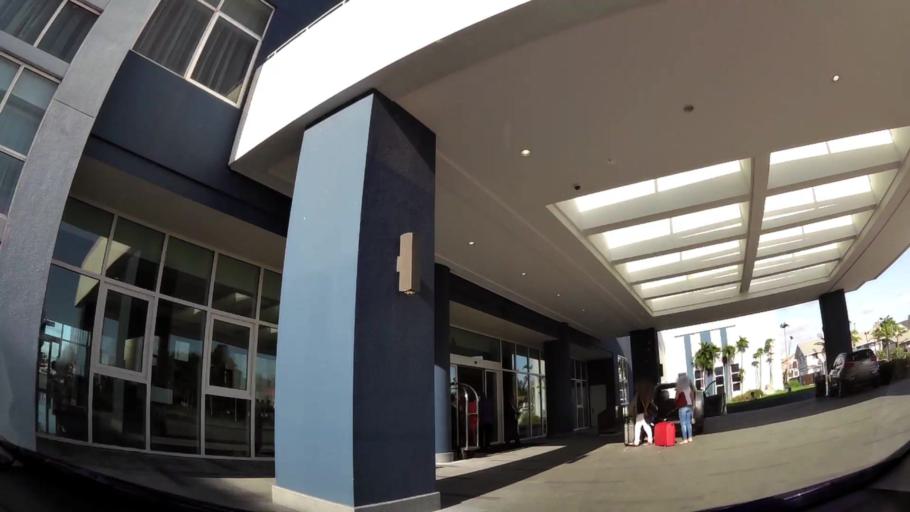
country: GY
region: Demerara-Mahaica
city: Georgetown
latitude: 6.8256
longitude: -58.1640
